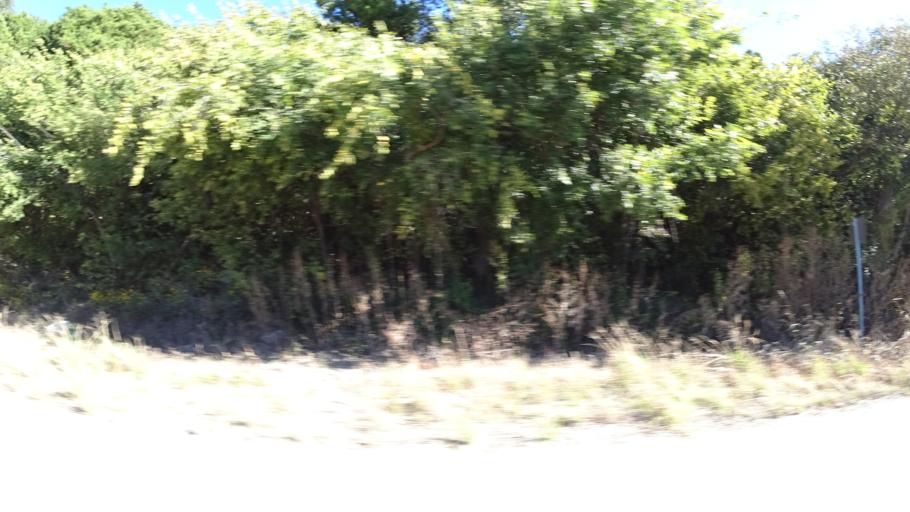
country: US
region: Texas
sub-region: Travis County
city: West Lake Hills
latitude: 30.3582
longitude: -97.7858
